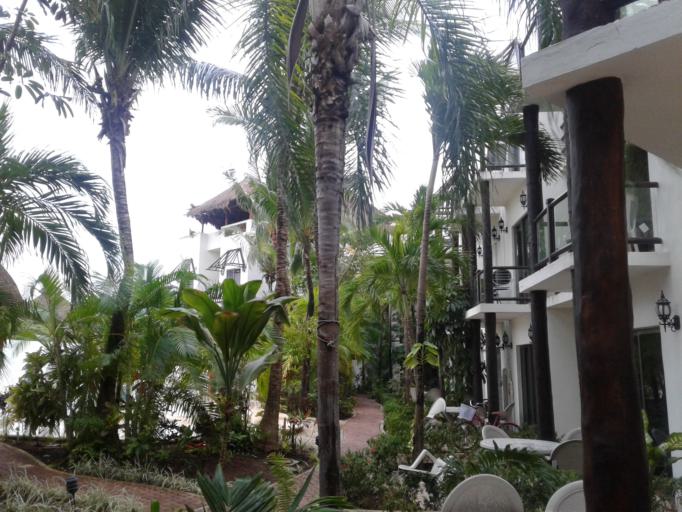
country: MX
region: Quintana Roo
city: Playa del Carmen
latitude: 20.6369
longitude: -87.0622
